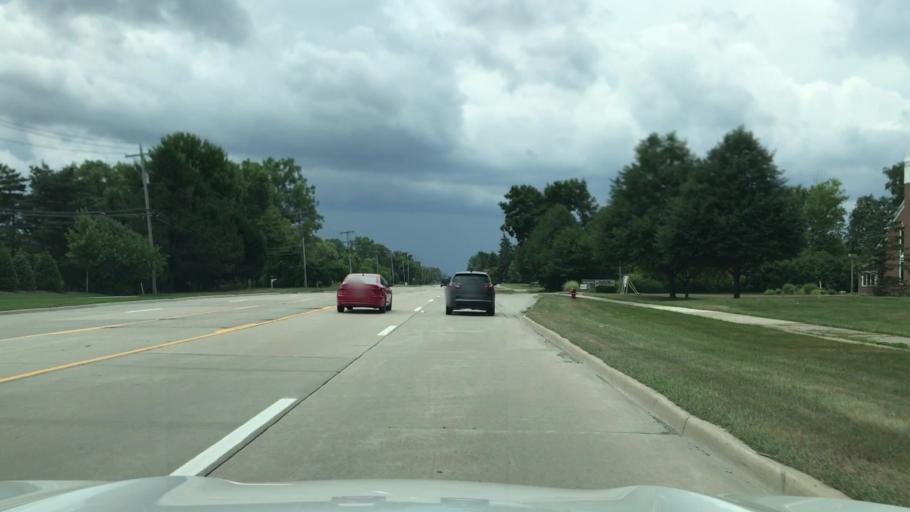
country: US
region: Michigan
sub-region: Oakland County
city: Troy
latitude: 42.5755
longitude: -83.1088
